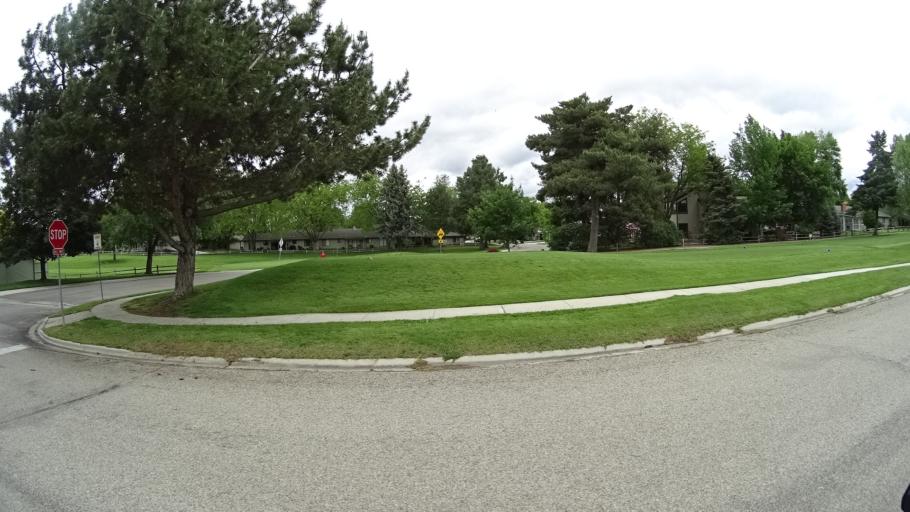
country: US
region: Idaho
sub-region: Ada County
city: Eagle
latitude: 43.7020
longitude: -116.3399
